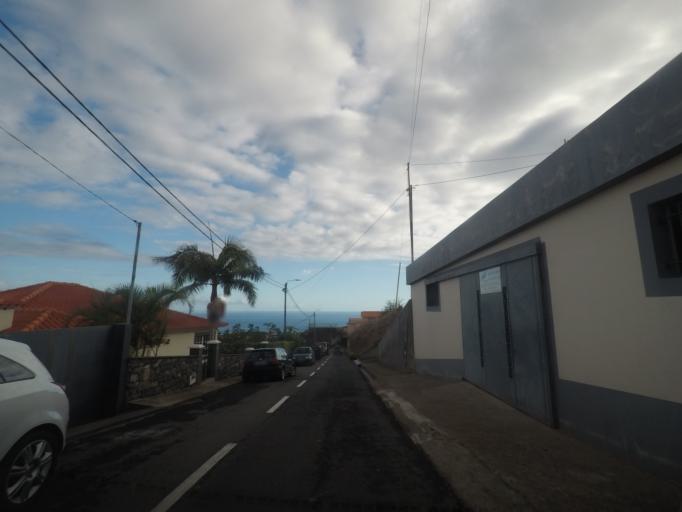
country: PT
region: Madeira
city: Camara de Lobos
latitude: 32.6534
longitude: -16.9923
